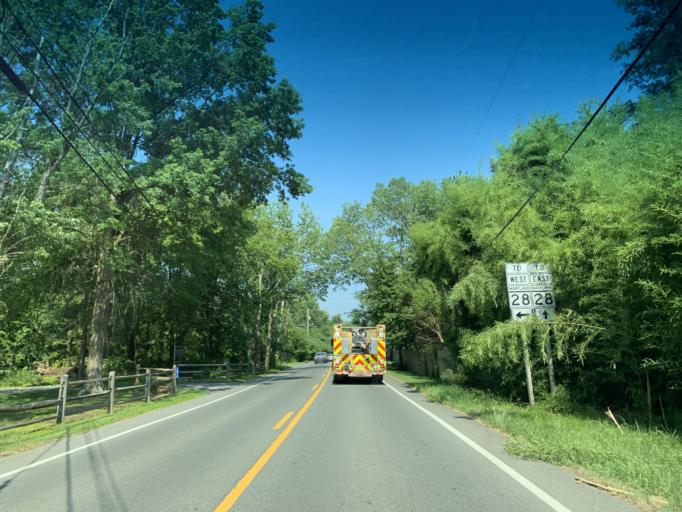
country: US
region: Maryland
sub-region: Montgomery County
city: Darnestown
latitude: 39.1282
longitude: -77.3478
